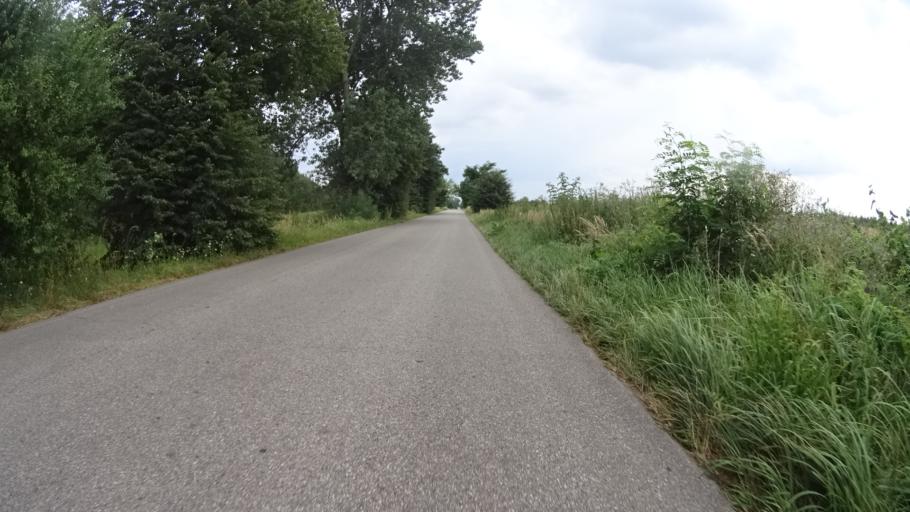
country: PL
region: Masovian Voivodeship
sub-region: Powiat grojecki
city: Goszczyn
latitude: 51.6766
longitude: 20.8590
